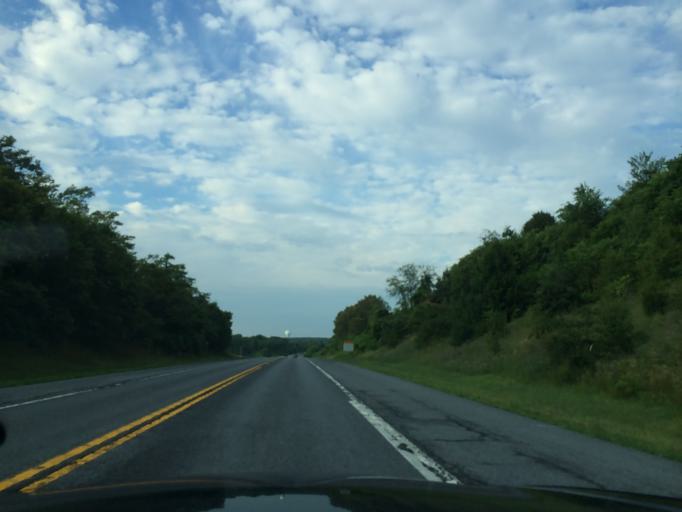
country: US
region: Maryland
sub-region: Carroll County
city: Mount Airy
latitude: 39.3902
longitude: -77.1412
